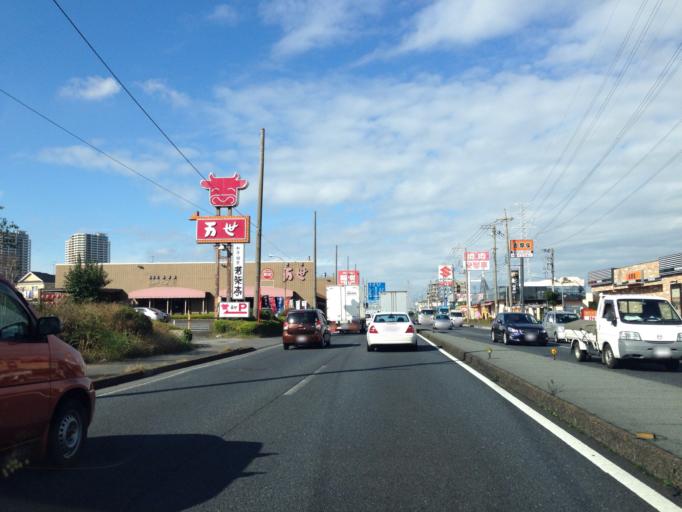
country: JP
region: Chiba
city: Kashiwa
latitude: 35.8878
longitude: 139.9620
